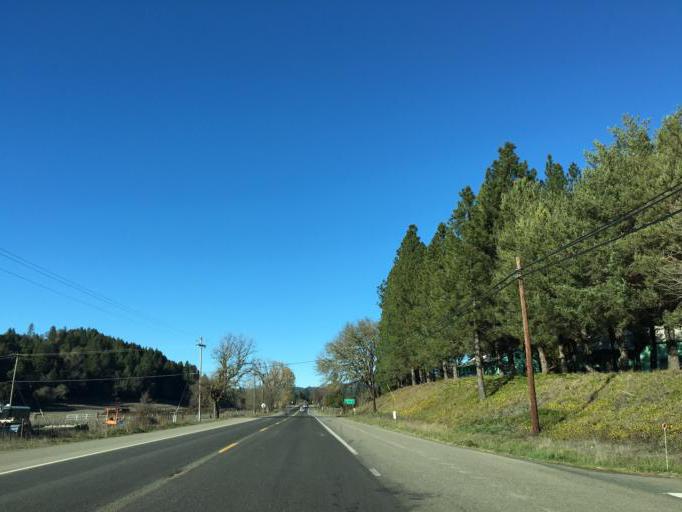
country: US
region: California
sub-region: Mendocino County
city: Laytonville
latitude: 39.7017
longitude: -123.4869
